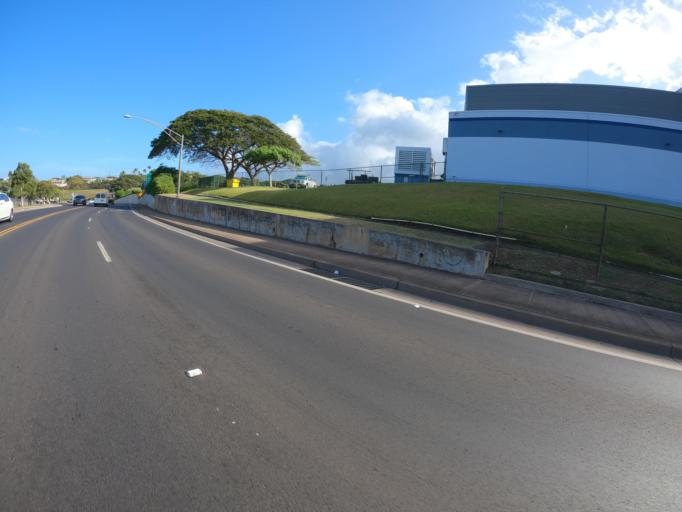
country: US
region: Hawaii
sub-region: Honolulu County
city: Halawa Heights
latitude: 21.3724
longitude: -157.9163
